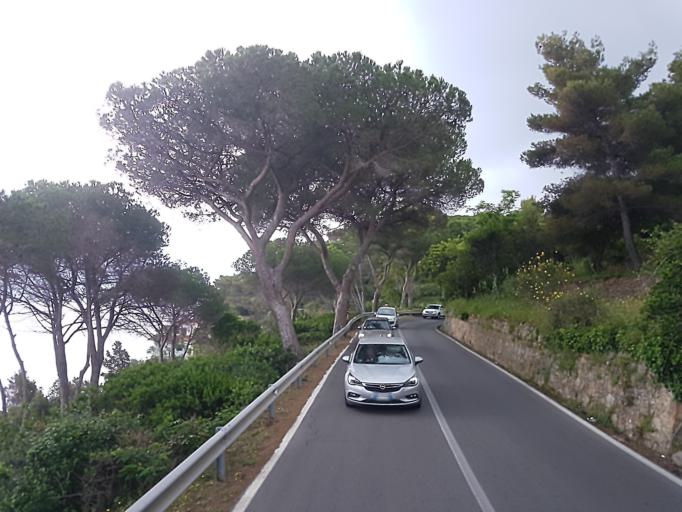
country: IT
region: Tuscany
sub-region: Provincia di Livorno
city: Marciana Marina
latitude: 42.8042
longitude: 10.2084
